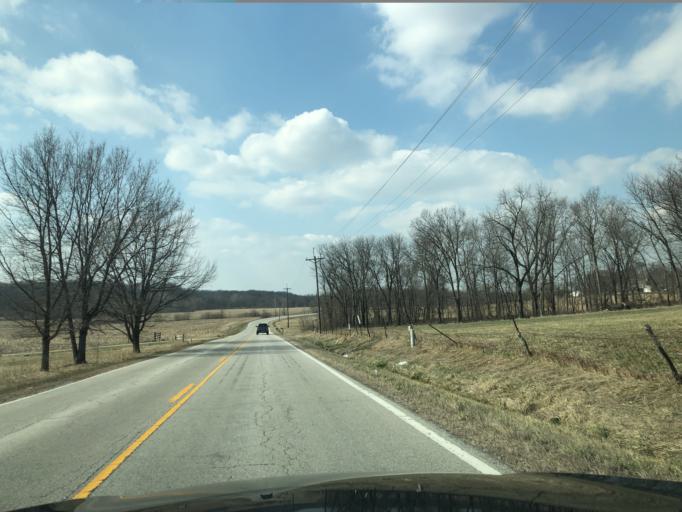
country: US
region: Missouri
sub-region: Platte County
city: Platte City
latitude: 39.4683
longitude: -94.8070
